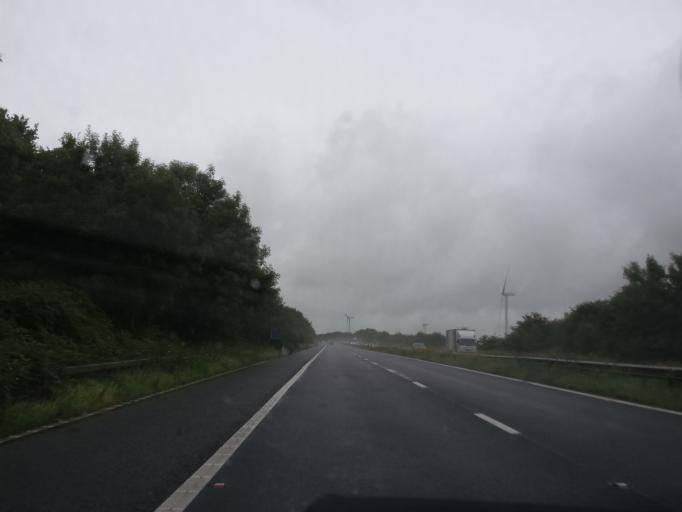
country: GB
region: England
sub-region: Rotherham
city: Bramley
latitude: 53.3910
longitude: -1.2742
